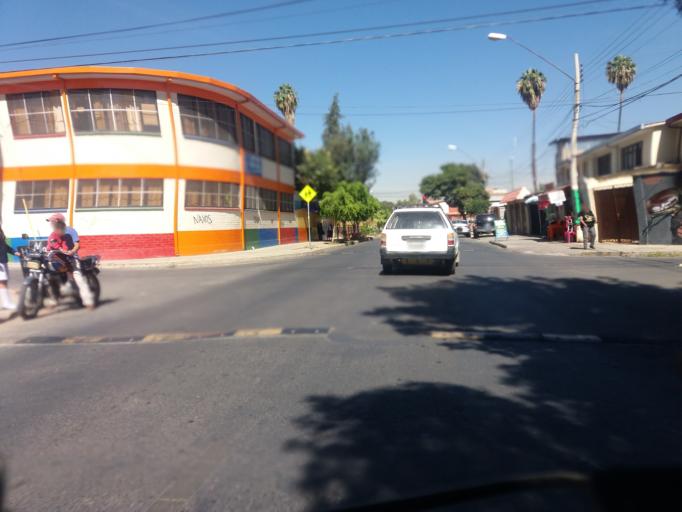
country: BO
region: Cochabamba
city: Cochabamba
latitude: -17.3890
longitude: -66.1439
